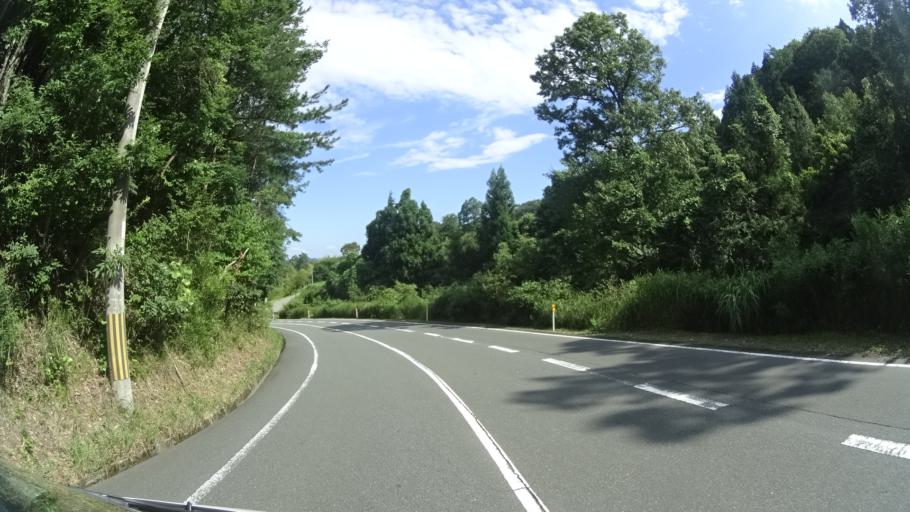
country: JP
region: Kyoto
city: Fukuchiyama
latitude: 35.3430
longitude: 135.1595
